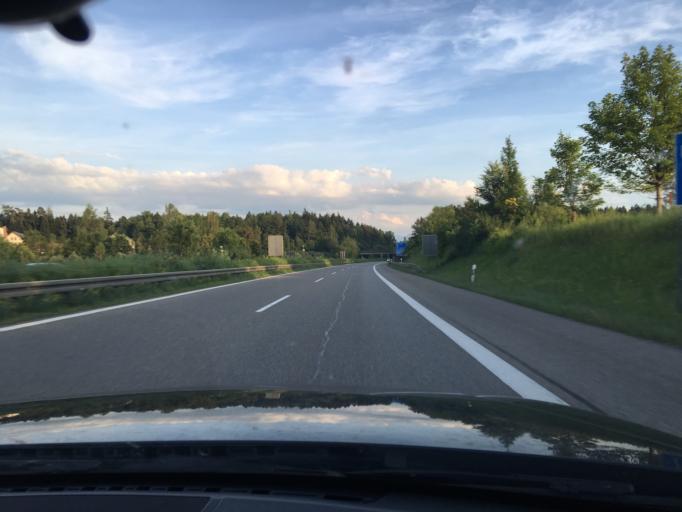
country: DE
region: Bavaria
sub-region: Swabia
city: Weissensberg
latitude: 47.5900
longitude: 9.7357
